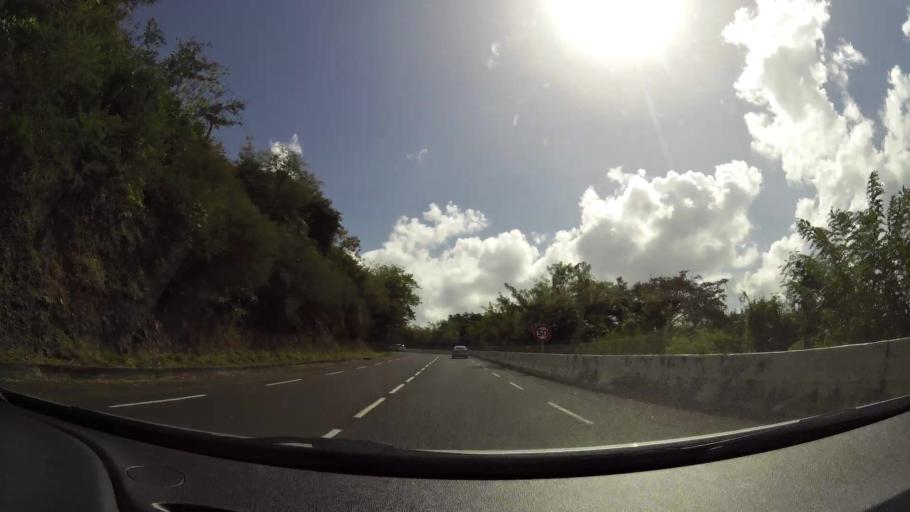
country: MQ
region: Martinique
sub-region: Martinique
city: Fort-de-France
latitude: 14.6338
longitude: -61.1295
